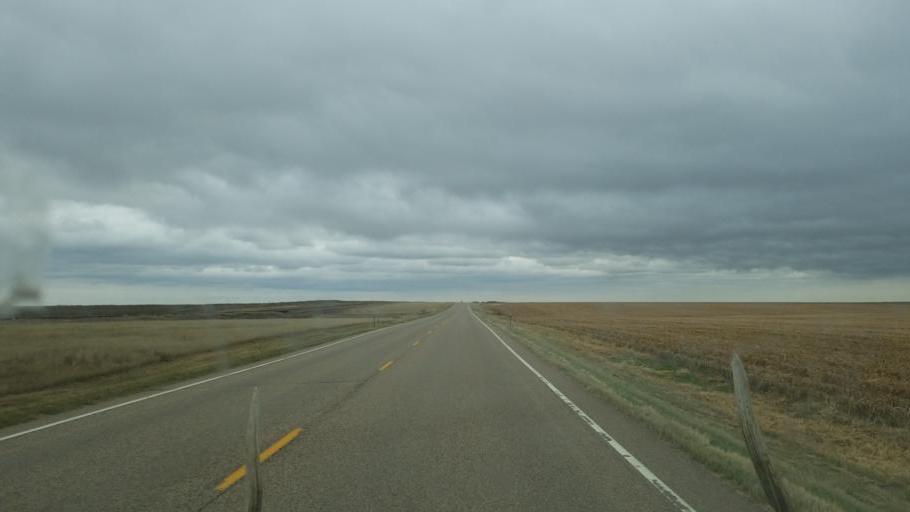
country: US
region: Colorado
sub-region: Cheyenne County
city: Cheyenne Wells
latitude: 38.8166
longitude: -102.5258
